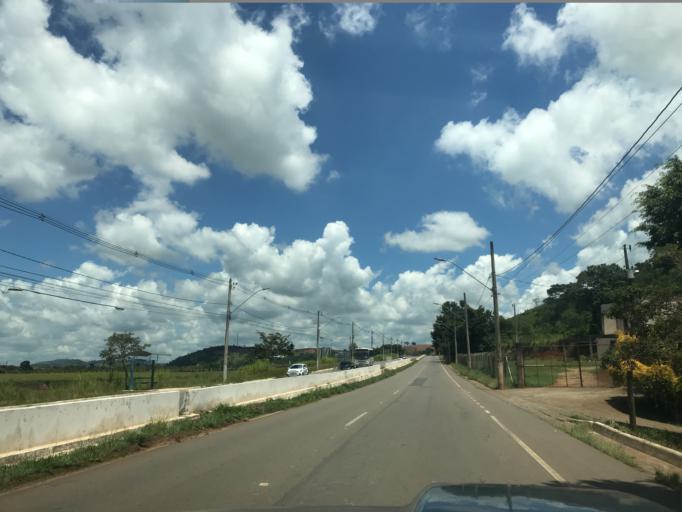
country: BR
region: Minas Gerais
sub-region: Tres Coracoes
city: Tres Coracoes
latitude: -21.6602
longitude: -45.2895
